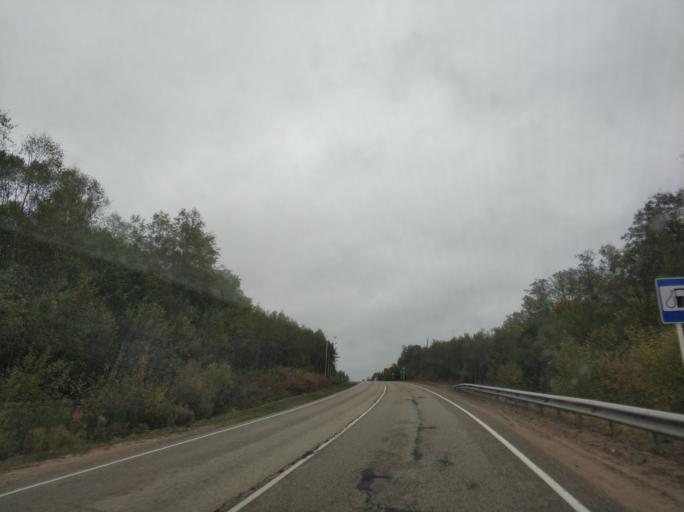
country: BY
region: Vitebsk
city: Rasony
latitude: 56.0611
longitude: 28.7151
